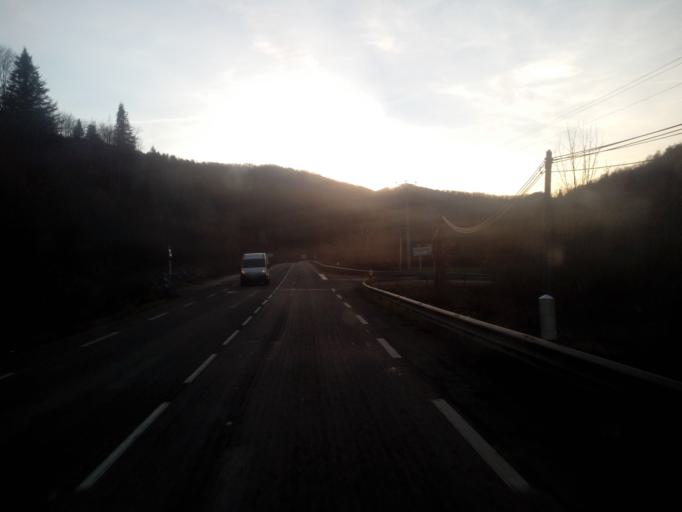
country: FR
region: Midi-Pyrenees
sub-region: Departement de l'Ariege
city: Lavelanet
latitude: 42.9153
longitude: 1.7944
